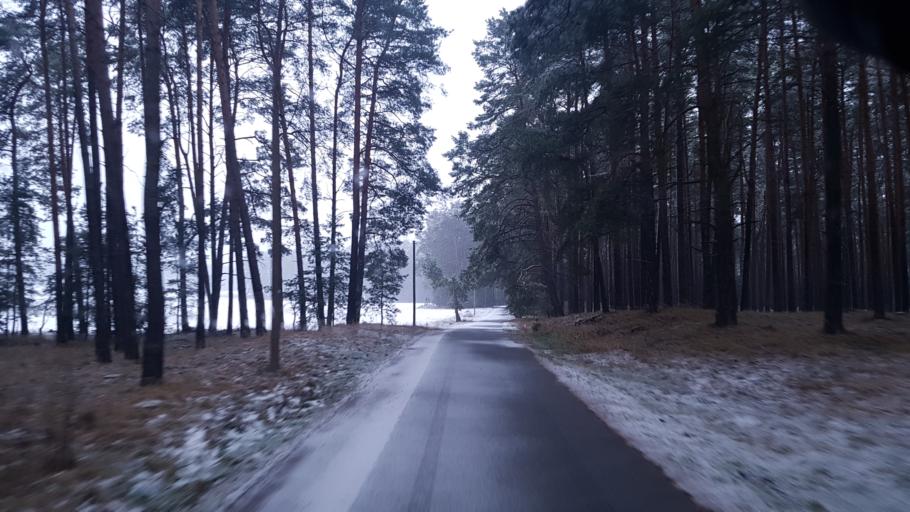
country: DE
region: Brandenburg
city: Schenkendobern
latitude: 51.9114
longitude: 14.5655
